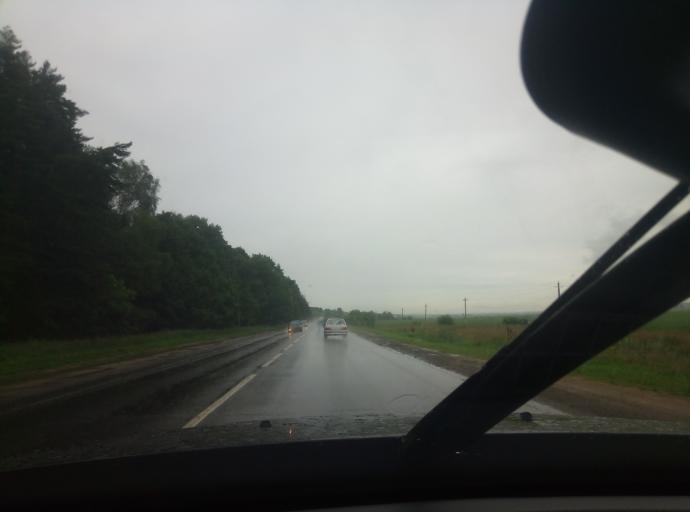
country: RU
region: Moskovskaya
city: Protvino
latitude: 54.8919
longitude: 37.3036
